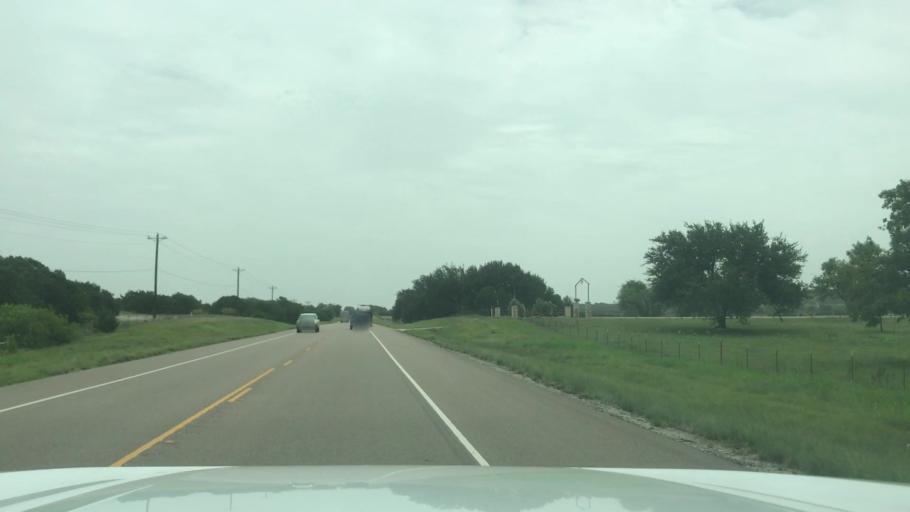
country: US
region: Texas
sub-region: Bosque County
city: Meridian
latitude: 31.9419
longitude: -97.7135
